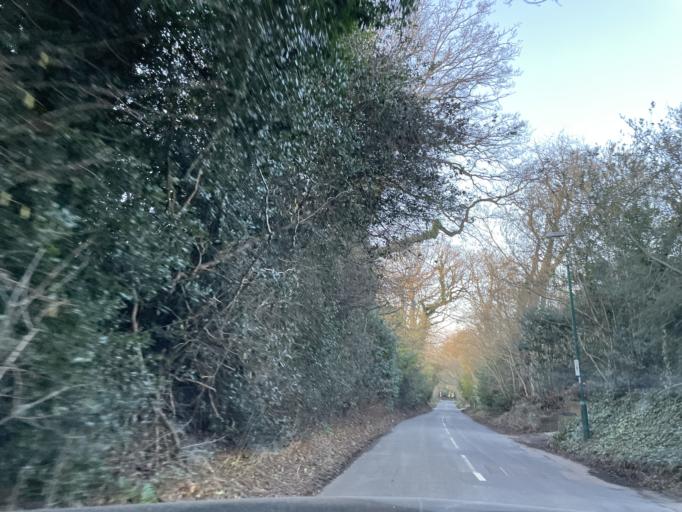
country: GB
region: England
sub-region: Kent
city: Westerham
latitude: 51.2706
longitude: 0.1264
